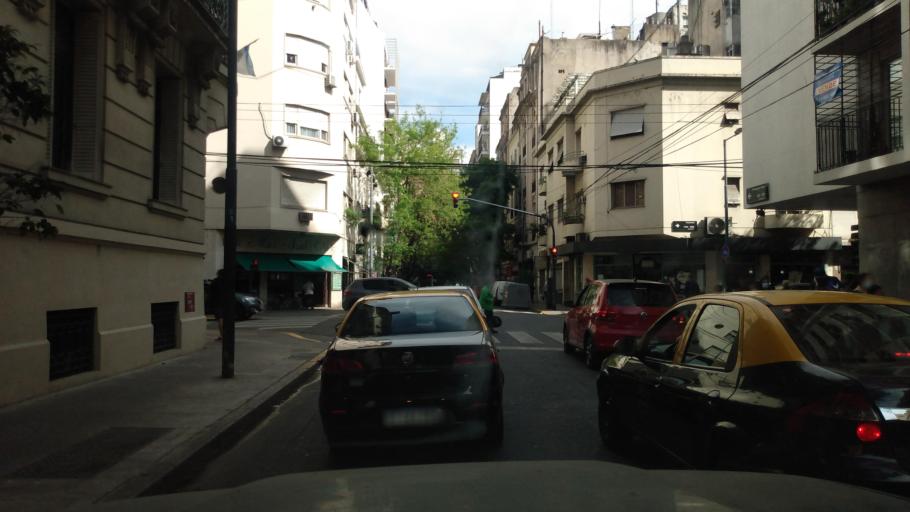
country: AR
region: Buenos Aires F.D.
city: Buenos Aires
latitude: -34.6017
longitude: -58.3914
